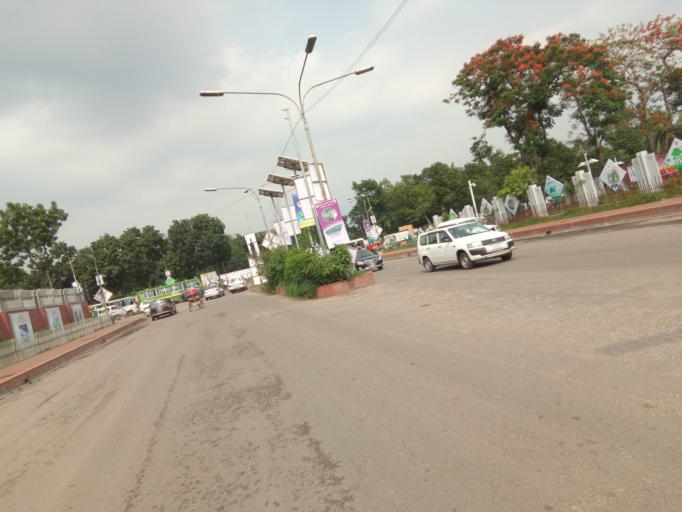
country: BD
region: Dhaka
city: Azimpur
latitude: 23.7707
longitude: 90.3817
